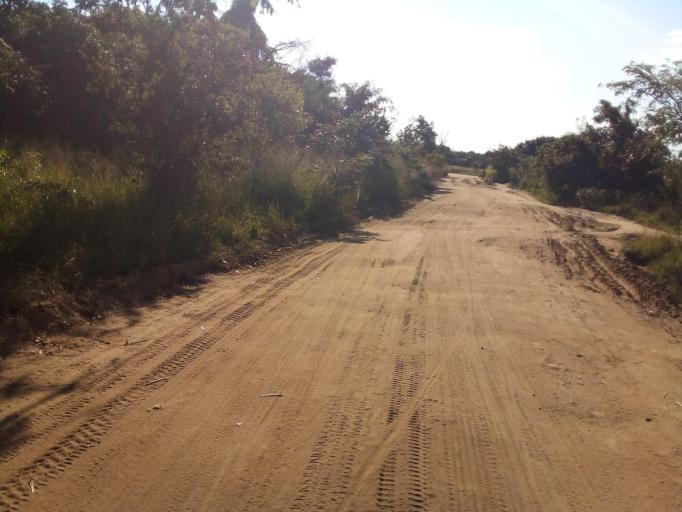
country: MZ
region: Zambezia
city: Quelimane
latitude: -17.5133
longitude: 36.8360
